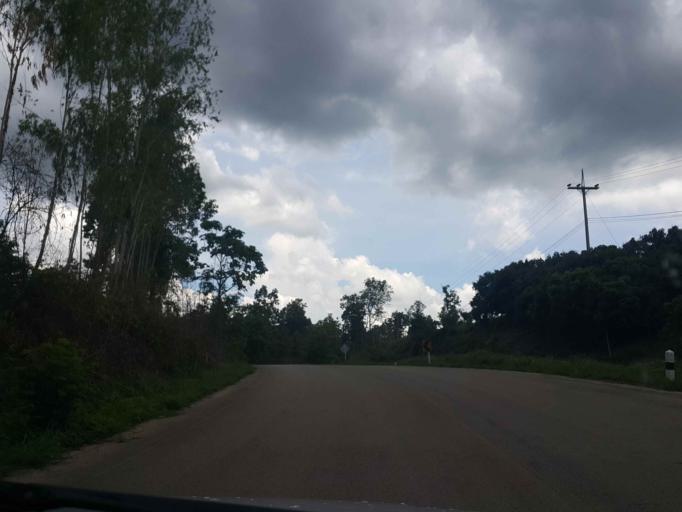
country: TH
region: Phayao
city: Dok Kham Tai
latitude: 18.9625
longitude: 100.0742
